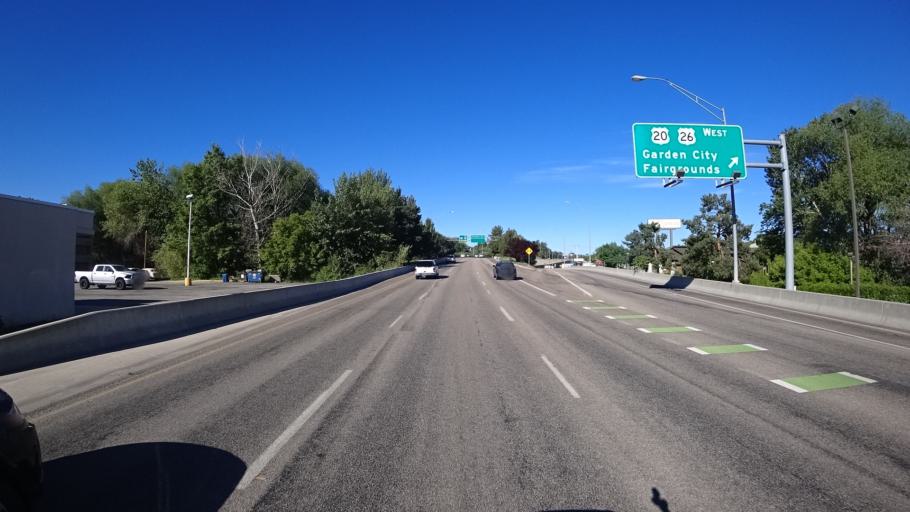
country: US
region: Idaho
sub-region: Ada County
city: Garden City
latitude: 43.6199
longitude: -116.2323
